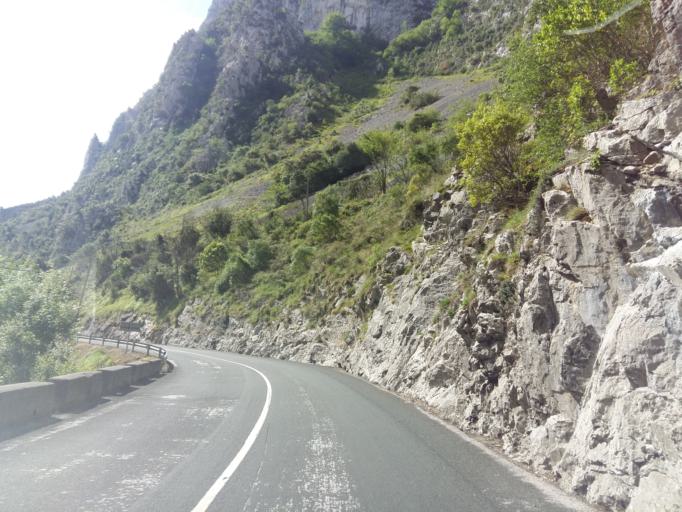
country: ES
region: Cantabria
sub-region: Provincia de Cantabria
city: Tresviso
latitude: 43.2668
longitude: -4.6316
